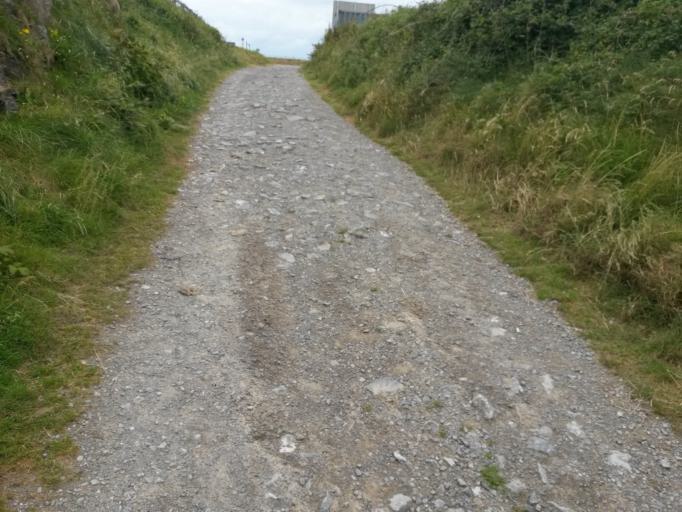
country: IE
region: Ulster
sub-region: County Donegal
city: Bundoran
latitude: 54.4904
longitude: -8.2661
